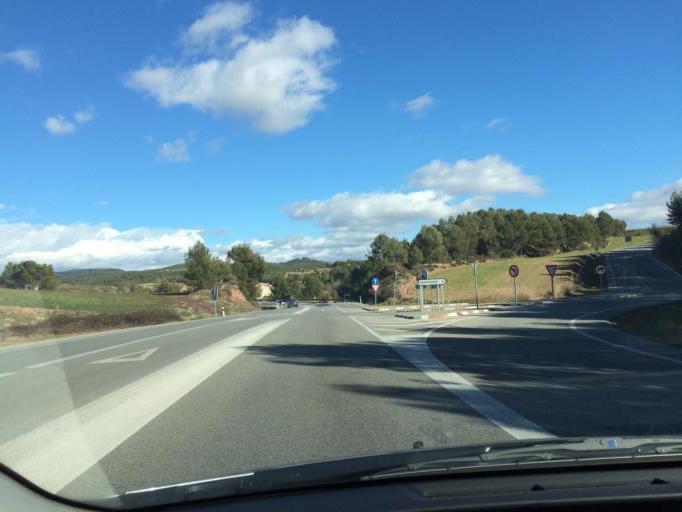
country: ES
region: Catalonia
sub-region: Provincia de Barcelona
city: Sant Joan de Vilatorrada
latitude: 41.7778
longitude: 1.7899
